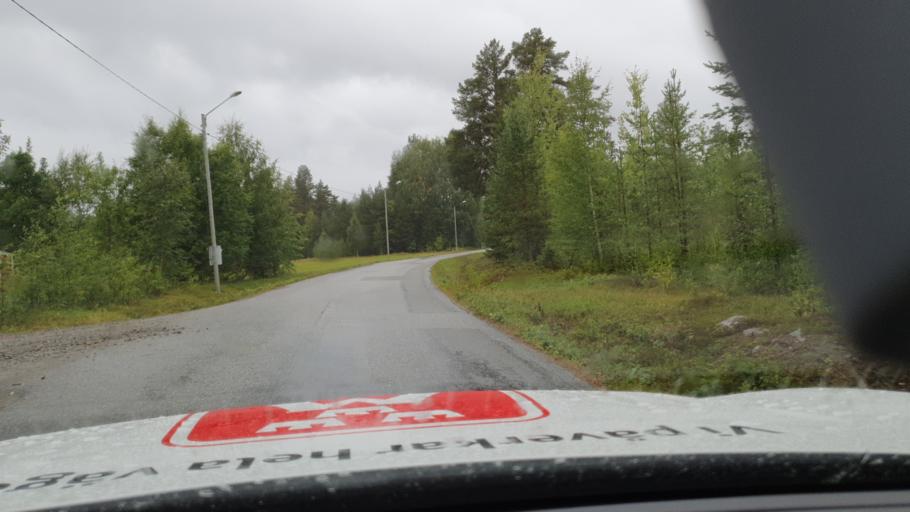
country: SE
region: Vaesterbotten
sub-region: Dorotea Kommun
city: Dorotea
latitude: 64.1069
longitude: 16.3329
